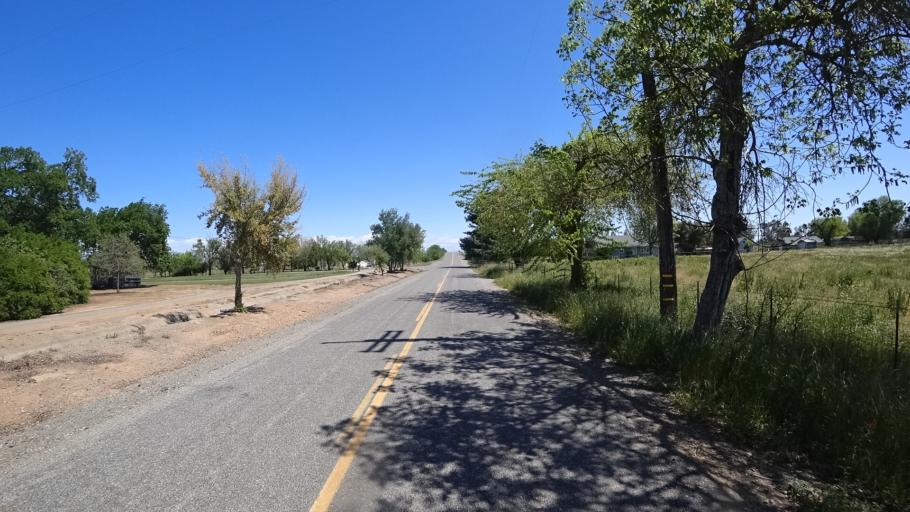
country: US
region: California
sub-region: Glenn County
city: Orland
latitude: 39.7945
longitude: -122.2058
